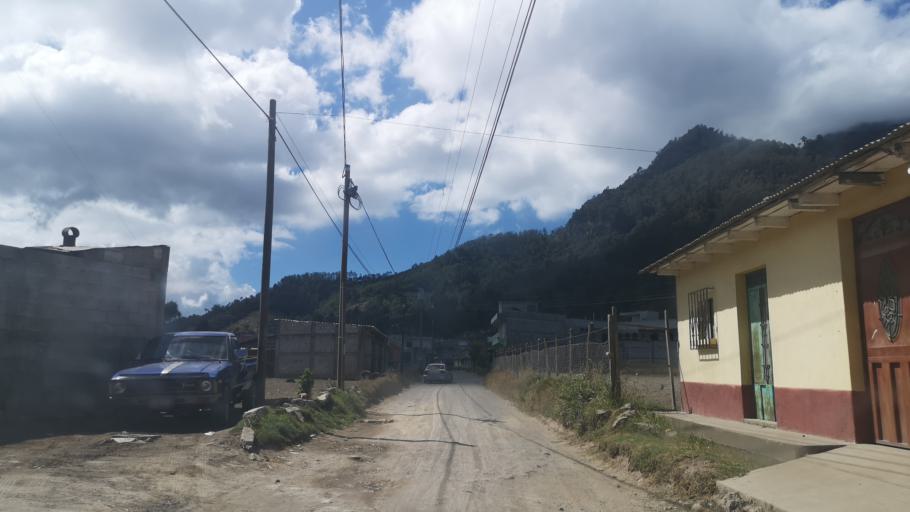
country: GT
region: Quetzaltenango
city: Almolonga
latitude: 14.7872
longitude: -91.5387
